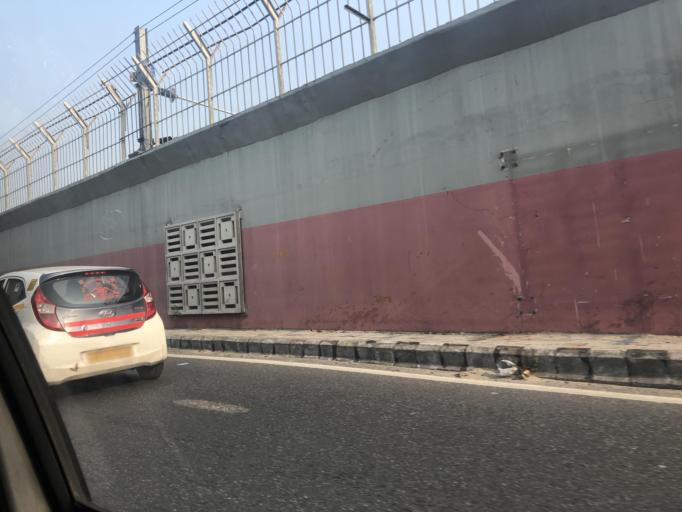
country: IN
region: NCT
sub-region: Central Delhi
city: Karol Bagh
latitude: 28.6127
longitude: 77.1372
